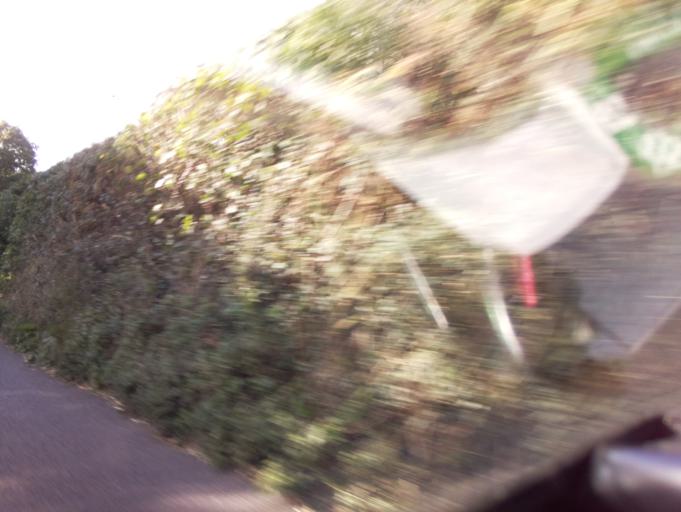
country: GB
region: England
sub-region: Devon
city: Newton Poppleford
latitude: 50.6998
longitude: -3.2788
